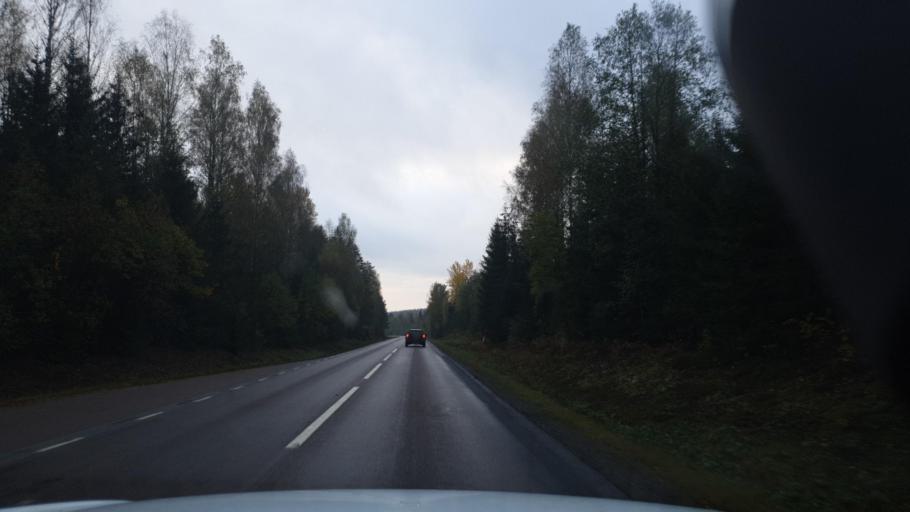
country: SE
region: Vaermland
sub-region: Arvika Kommun
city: Arvika
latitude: 59.6439
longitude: 12.7816
